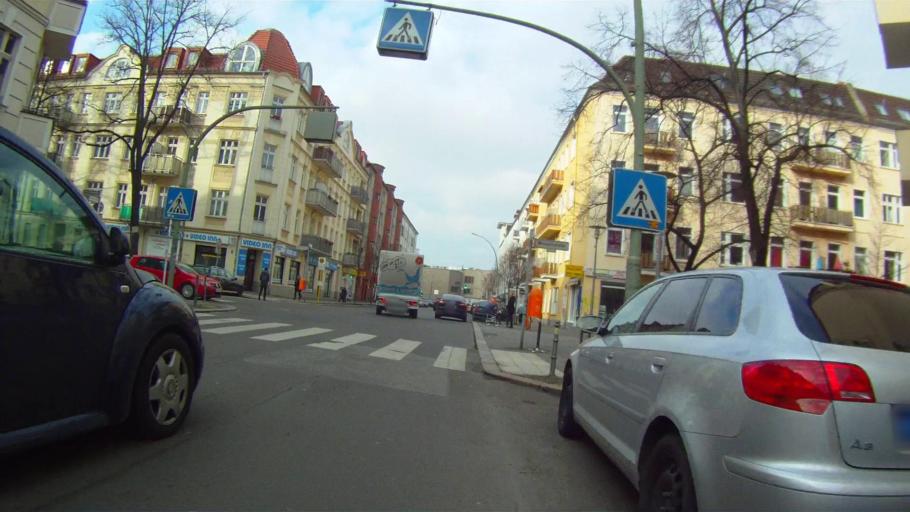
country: DE
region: Berlin
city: Lichtenberg
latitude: 52.5094
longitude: 13.5001
